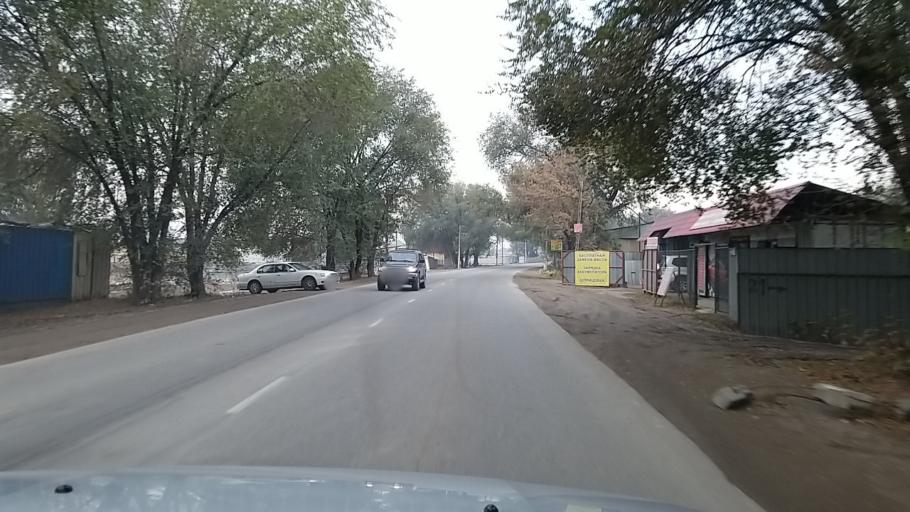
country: KZ
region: Almaty Oblysy
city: Burunday
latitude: 43.3527
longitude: 76.8279
